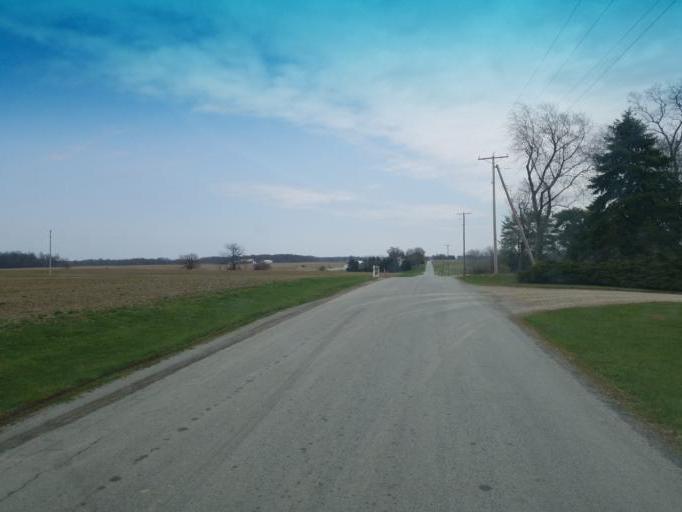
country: US
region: Ohio
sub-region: Wyandot County
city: Upper Sandusky
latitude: 40.8622
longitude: -83.2012
